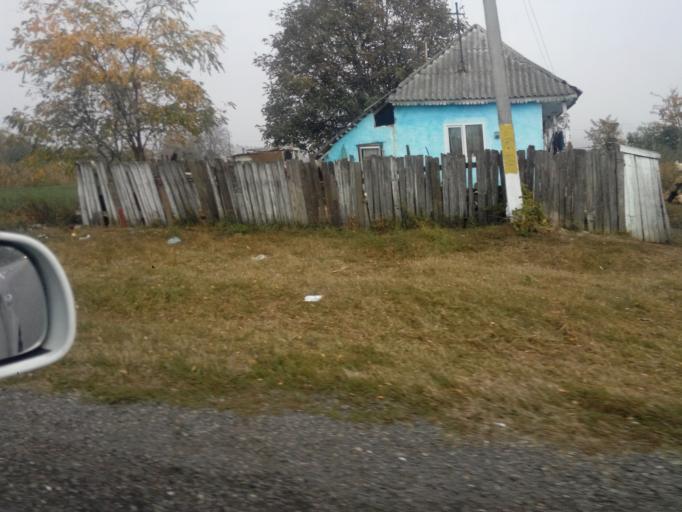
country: RO
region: Bacau
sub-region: Comuna Urechesti
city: Urechesti
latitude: 46.1282
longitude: 27.1001
